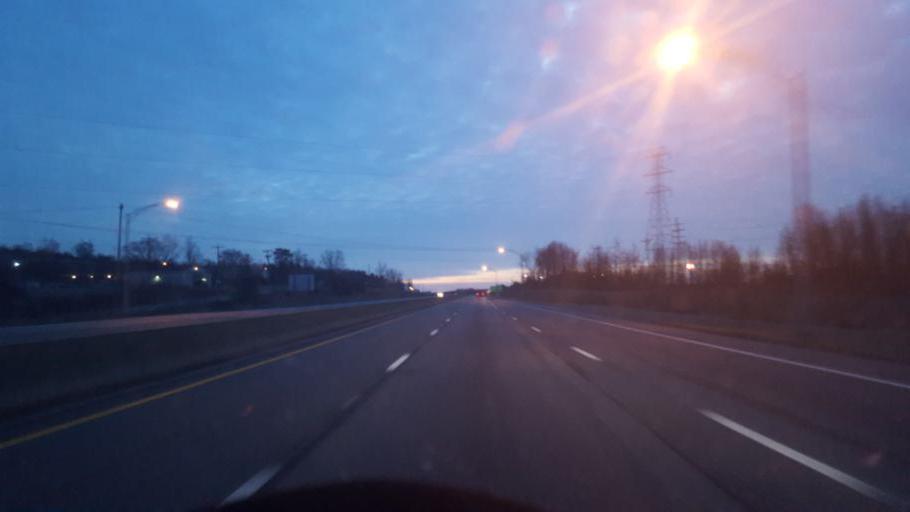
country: US
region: Ohio
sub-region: Jackson County
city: Jackson
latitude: 39.0424
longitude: -82.6094
